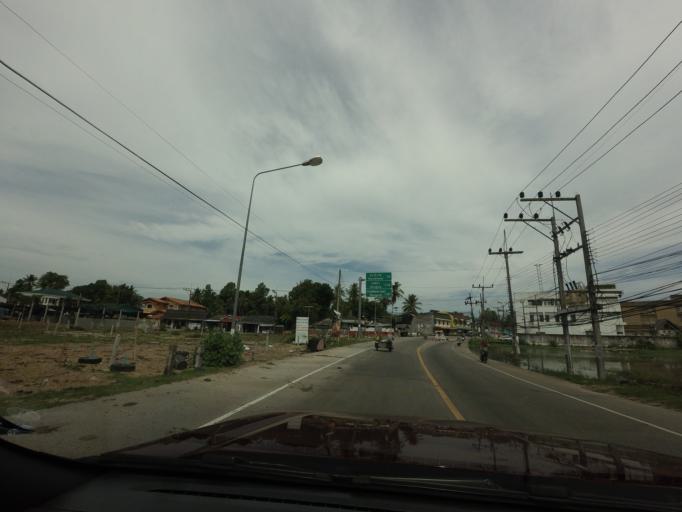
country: TH
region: Narathiwat
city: Tak Bai
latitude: 6.2381
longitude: 102.0847
